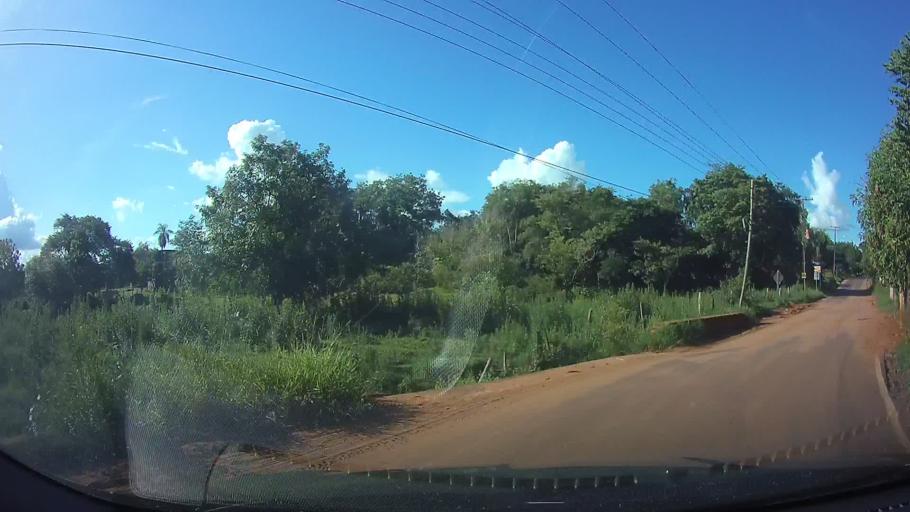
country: PY
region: Central
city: Itaugua
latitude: -25.3704
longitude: -57.3687
